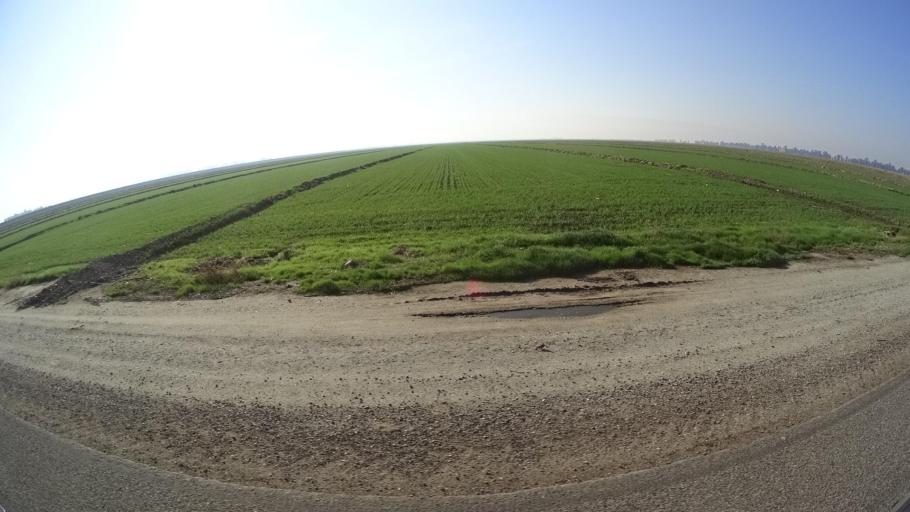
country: US
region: California
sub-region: Kern County
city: Greenfield
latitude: 35.2086
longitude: -118.9808
